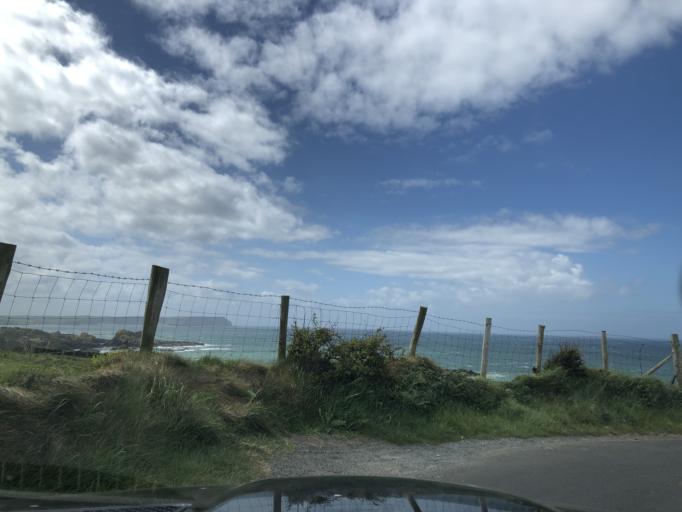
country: GB
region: Northern Ireland
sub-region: Moyle District
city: Ballycastle
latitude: 55.2433
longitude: -6.3686
